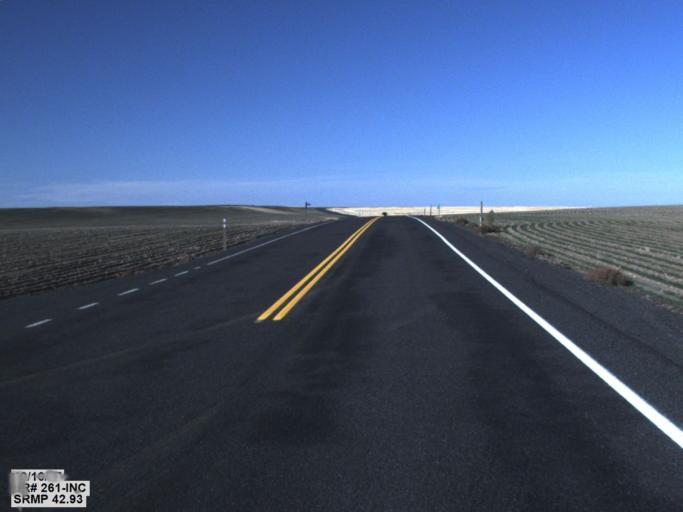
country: US
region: Washington
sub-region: Adams County
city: Ritzville
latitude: 46.8414
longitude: -118.3327
